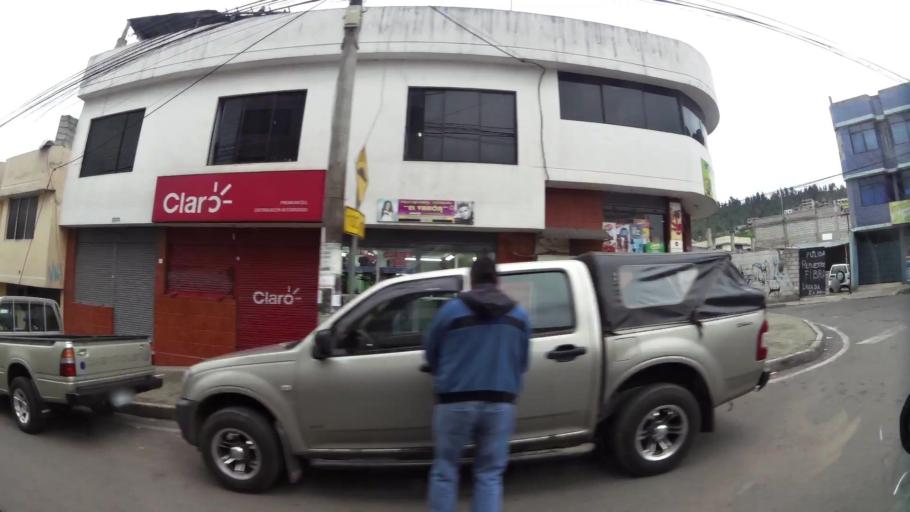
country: EC
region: Pichincha
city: Sangolqui
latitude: -0.3191
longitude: -78.5343
